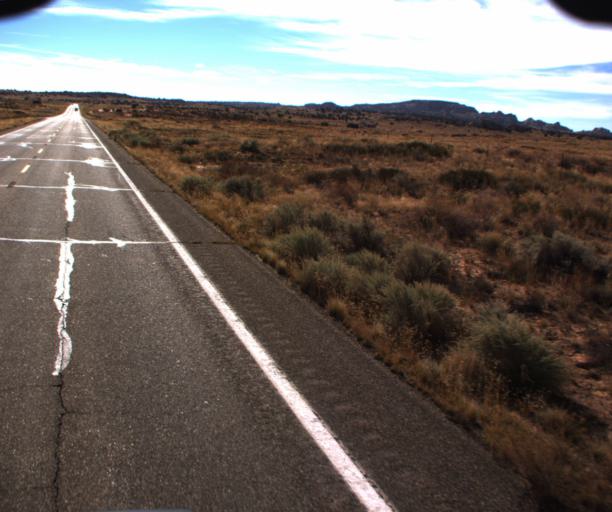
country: US
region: Arizona
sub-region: Coconino County
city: Kaibito
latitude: 36.5895
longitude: -111.1557
